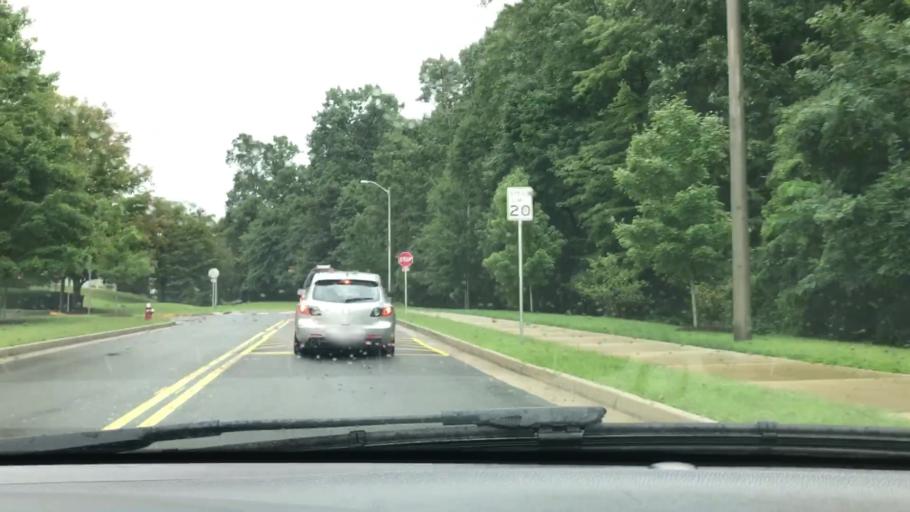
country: US
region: Virginia
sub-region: Fairfax County
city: Merrifield
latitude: 38.8611
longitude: -77.2326
